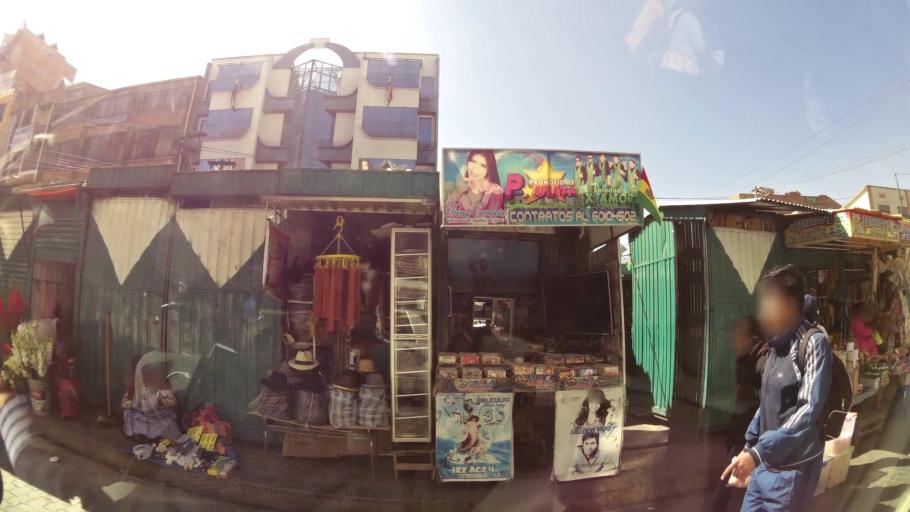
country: BO
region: La Paz
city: La Paz
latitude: -16.5061
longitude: -68.1607
